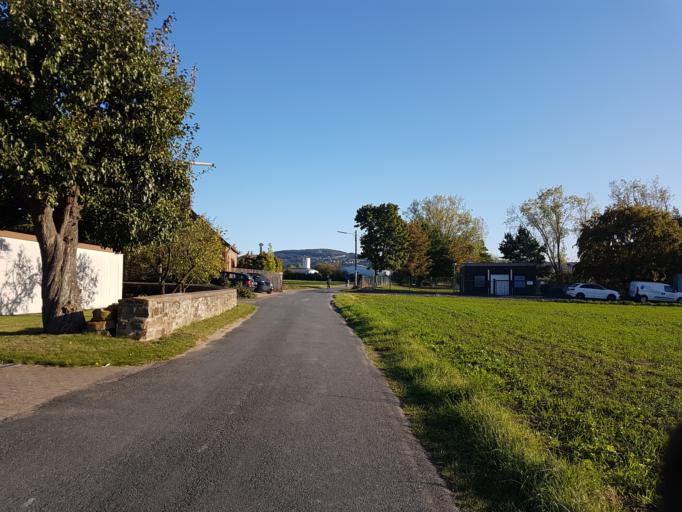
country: DE
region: North Rhine-Westphalia
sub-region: Regierungsbezirk Detmold
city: Vlotho
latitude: 52.1847
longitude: 8.8659
